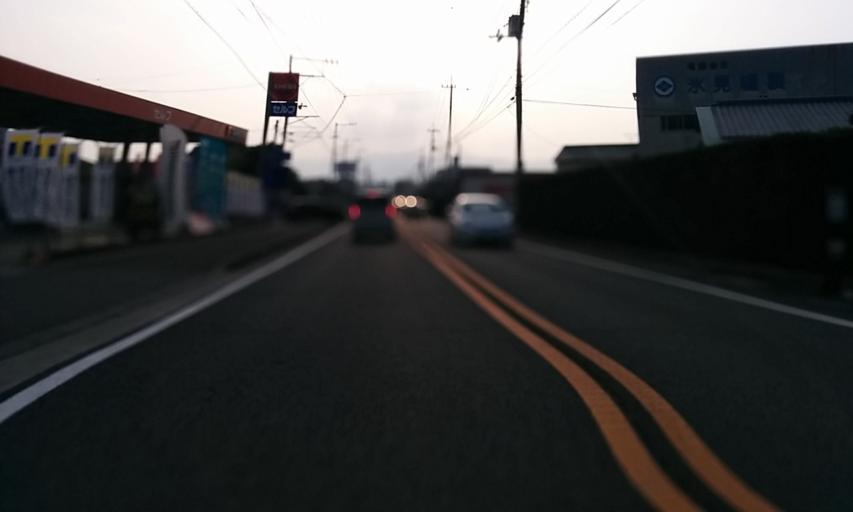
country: JP
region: Ehime
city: Saijo
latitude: 33.8953
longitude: 133.1355
